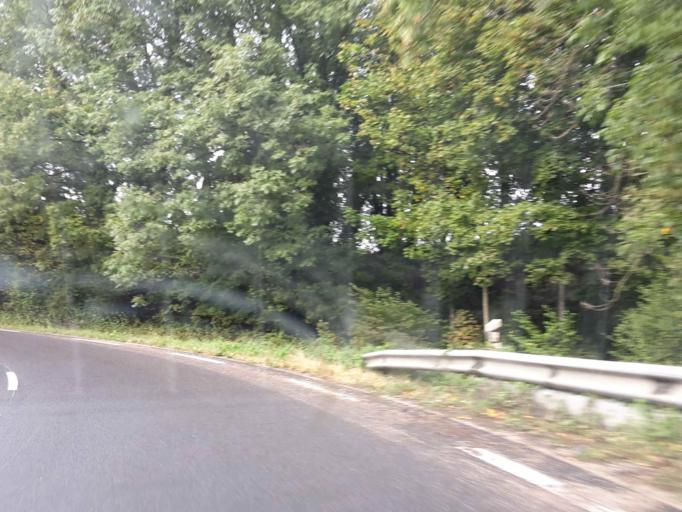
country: FR
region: Franche-Comte
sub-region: Departement du Doubs
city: Baume-les-Dames
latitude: 47.3495
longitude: 6.3437
